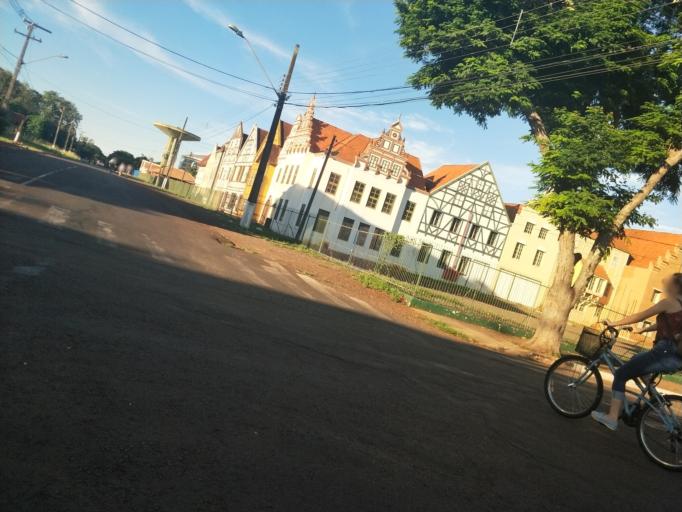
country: BR
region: Parana
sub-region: Marechal Candido Rondon
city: Marechal Candido Rondon
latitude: -24.5537
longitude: -54.0518
